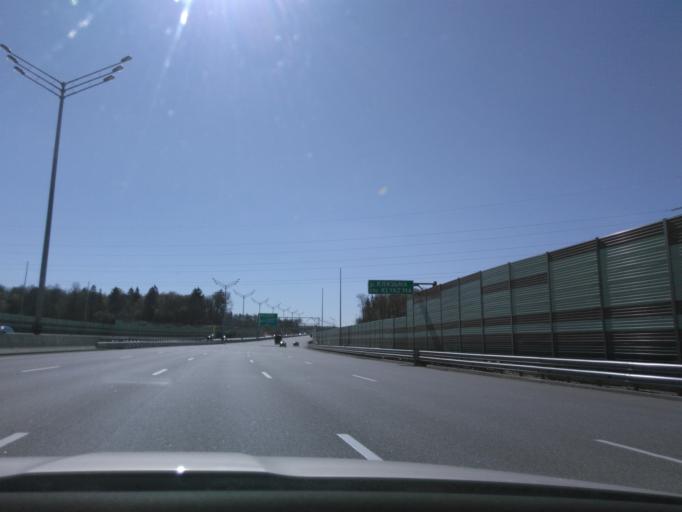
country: RU
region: Moscow
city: Khimki
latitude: 55.9546
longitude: 37.4279
